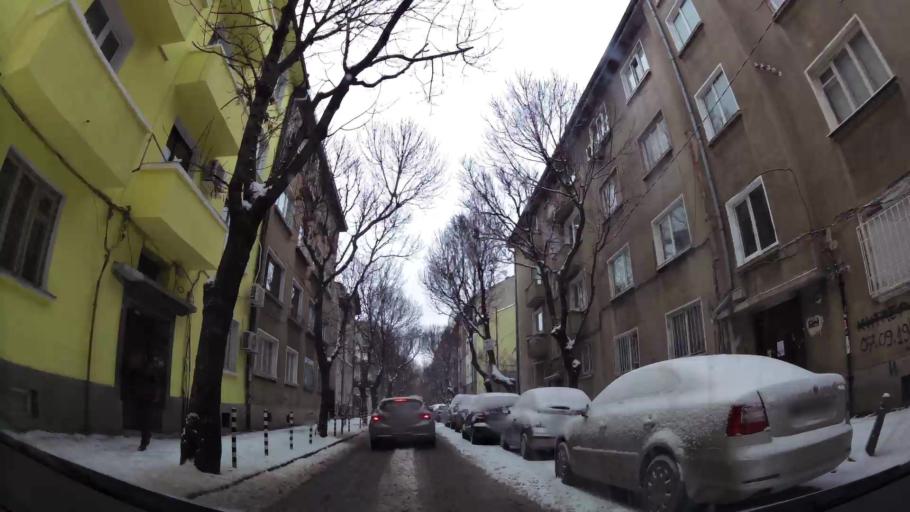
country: BG
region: Sofia-Capital
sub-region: Stolichna Obshtina
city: Sofia
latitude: 42.6898
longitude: 23.3111
